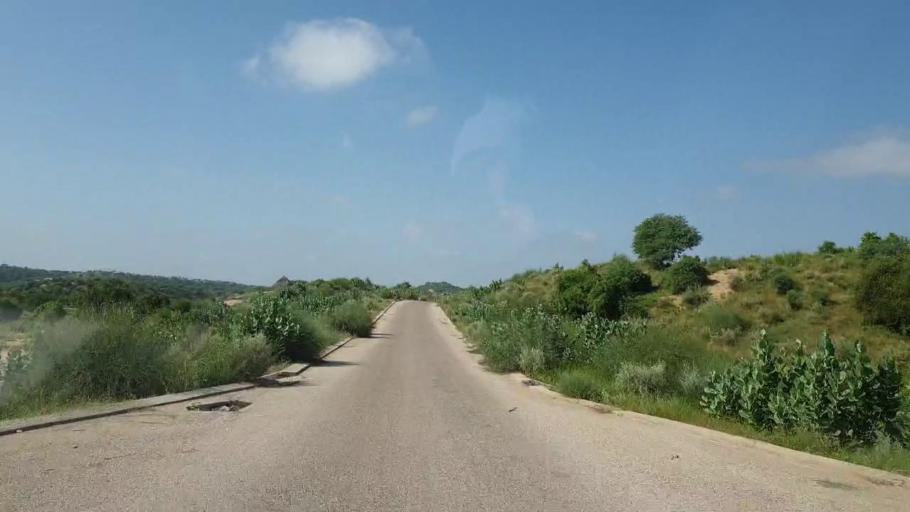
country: PK
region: Sindh
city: Mithi
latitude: 24.5535
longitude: 69.8917
